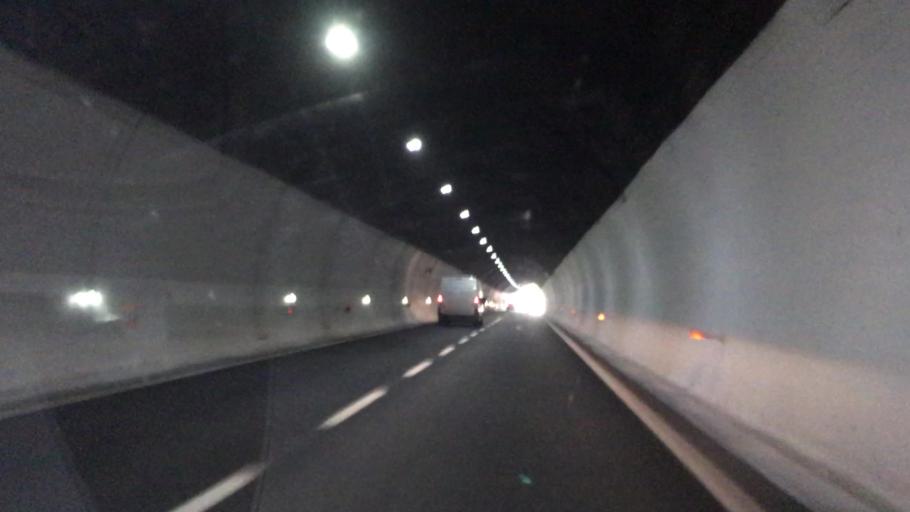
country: IT
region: Liguria
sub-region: Provincia di Genova
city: Cogorno
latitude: 44.3025
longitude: 9.3742
